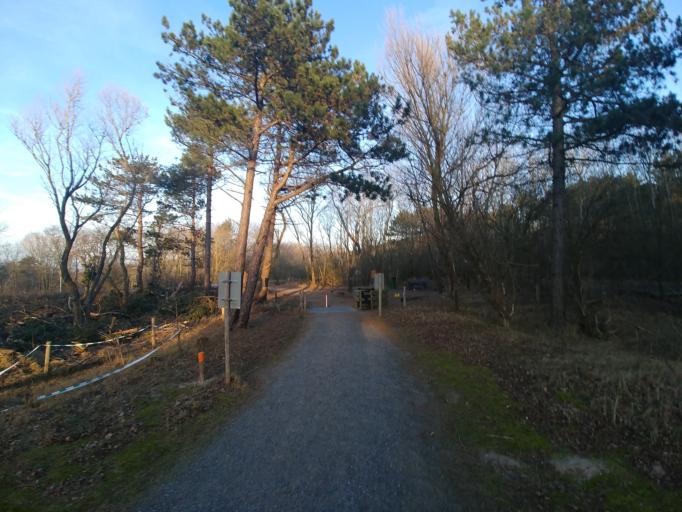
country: NL
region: South Holland
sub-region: Gemeente Wassenaar
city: Wassenaar
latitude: 52.1598
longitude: 4.3540
